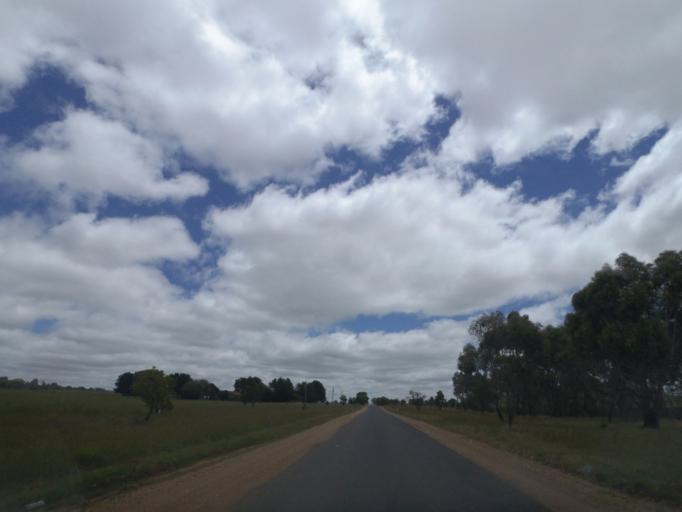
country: AU
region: Victoria
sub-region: Moorabool
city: Bacchus Marsh
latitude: -37.6196
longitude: 144.2549
